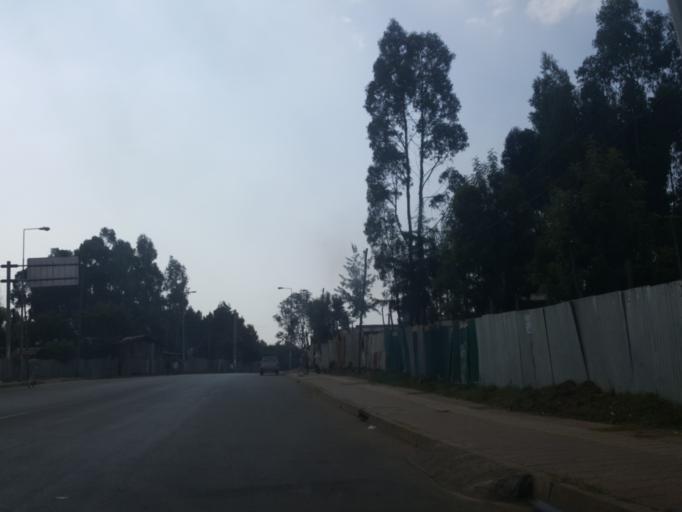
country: ET
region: Adis Abeba
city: Addis Ababa
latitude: 9.0675
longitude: 38.7212
